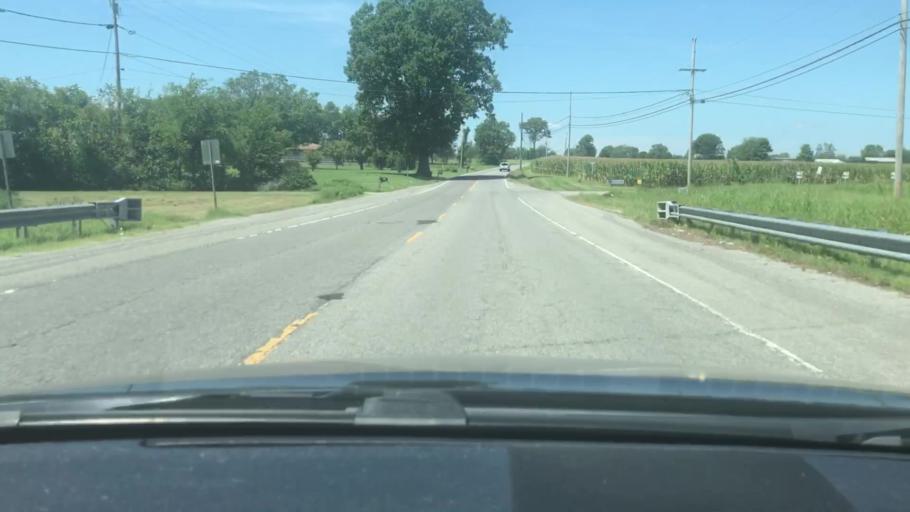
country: US
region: Tennessee
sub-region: Sumner County
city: Gallatin
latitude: 36.4015
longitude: -86.4880
